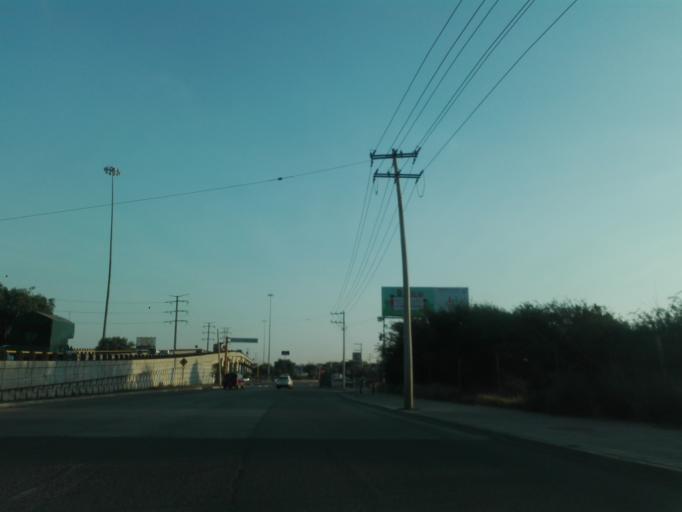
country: MX
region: Guanajuato
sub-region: Leon
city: Medina
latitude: 21.1287
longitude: -101.6297
